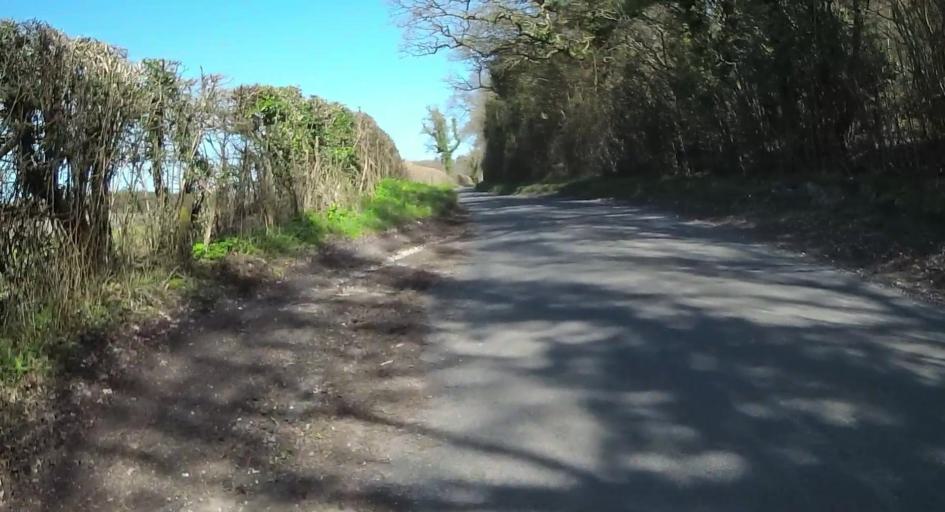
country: GB
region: England
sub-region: Hampshire
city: Overton
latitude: 51.2686
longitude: -1.1963
